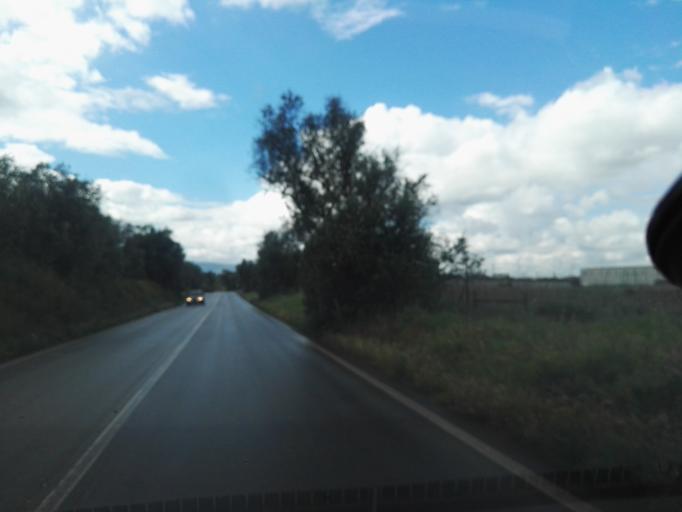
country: PT
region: Santarem
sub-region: Golega
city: Golega
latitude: 39.4253
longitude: -8.4987
